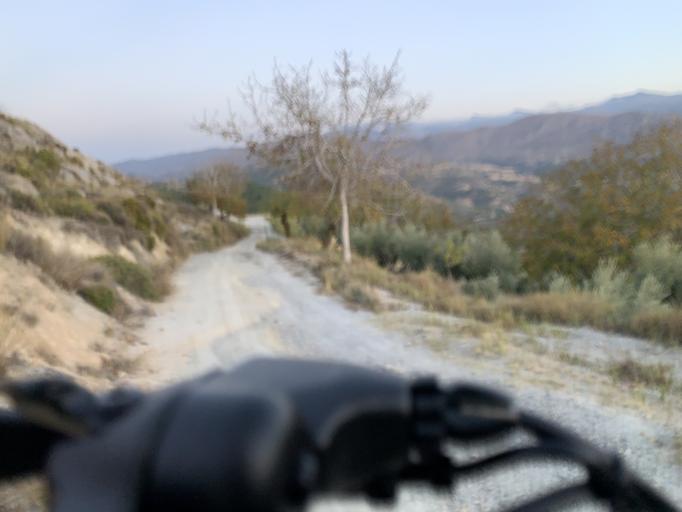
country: ES
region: Andalusia
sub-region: Provincia de Granada
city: Beas de Granada
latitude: 37.2224
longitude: -3.4589
